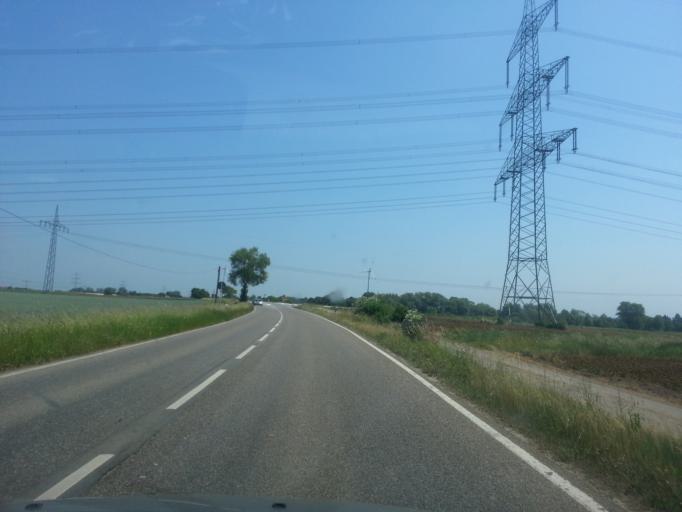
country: DE
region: Rheinland-Pfalz
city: Lambsheim
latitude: 49.5208
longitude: 8.2930
